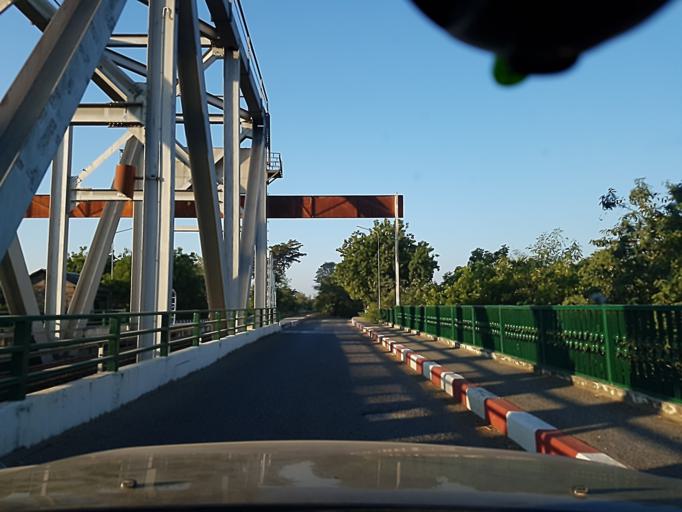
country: MM
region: Sagain
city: Monywa
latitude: 21.8018
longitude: 95.1677
